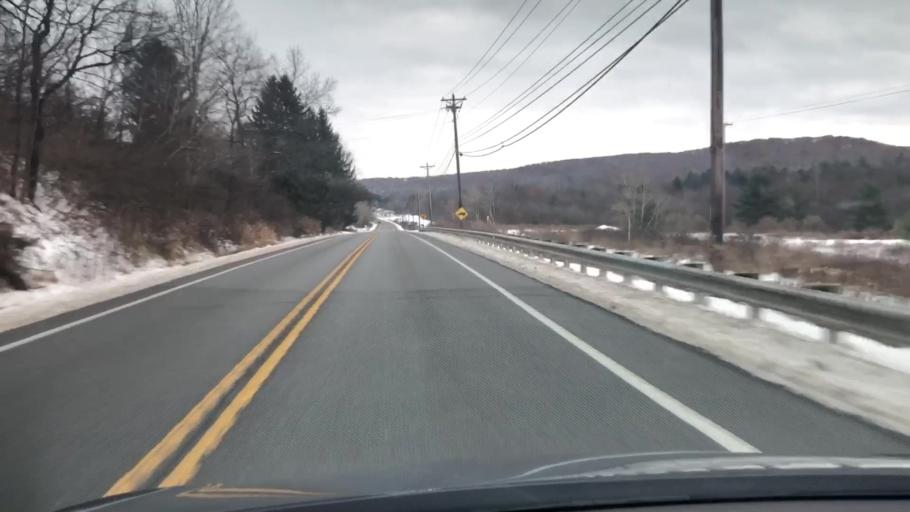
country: US
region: Pennsylvania
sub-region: Clearfield County
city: Treasure Lake
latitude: 41.1390
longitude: -78.6908
